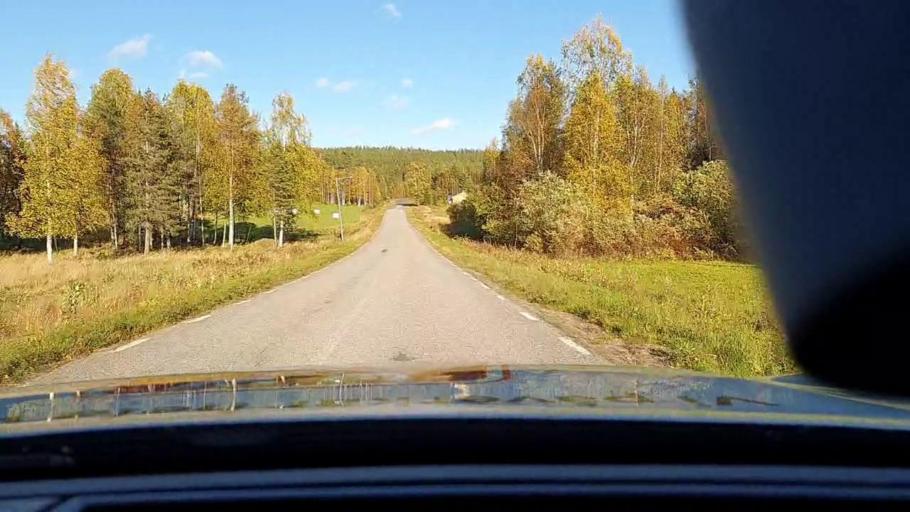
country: SE
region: Norrbotten
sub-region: Pitea Kommun
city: Norrfjarden
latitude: 65.6476
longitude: 21.5061
